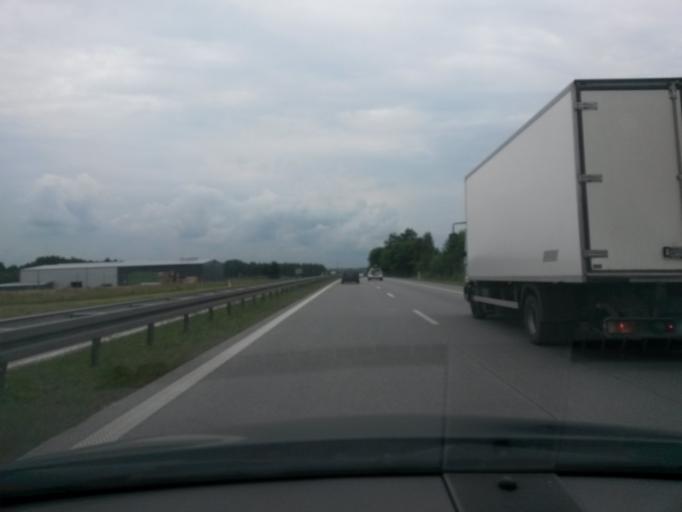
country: PL
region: Lodz Voivodeship
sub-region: Powiat skierniewicki
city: Kowiesy
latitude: 51.9009
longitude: 20.4332
